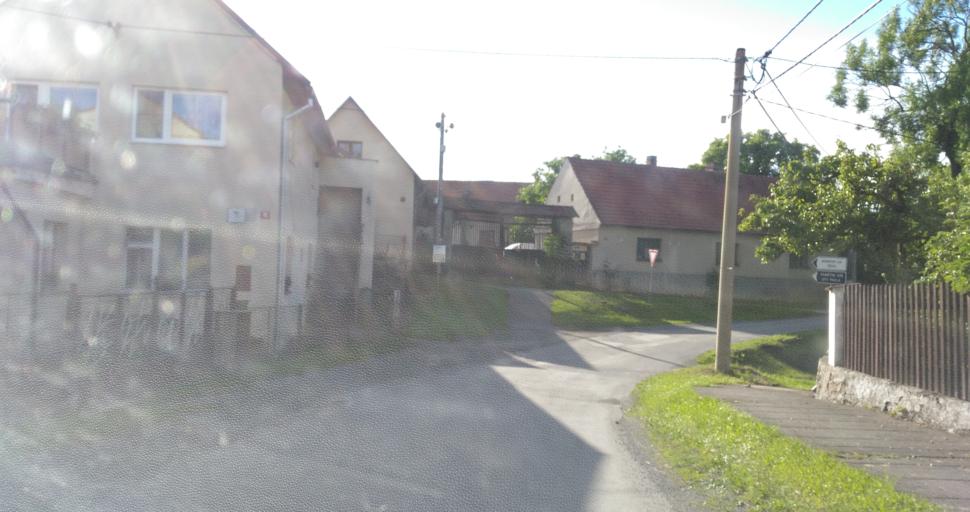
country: CZ
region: Central Bohemia
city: Roztoky
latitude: 50.0130
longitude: 13.8426
